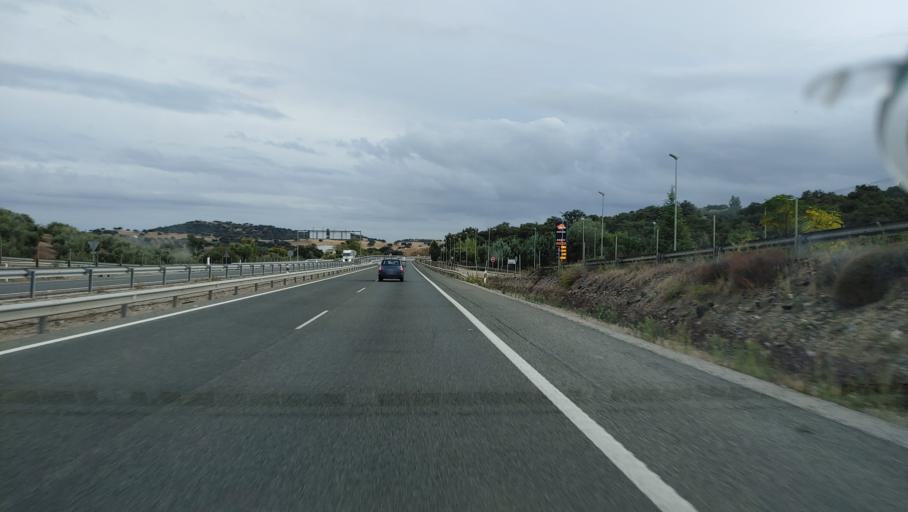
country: ES
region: Andalusia
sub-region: Provincia de Jaen
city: Santa Elena
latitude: 38.3376
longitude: -3.5447
